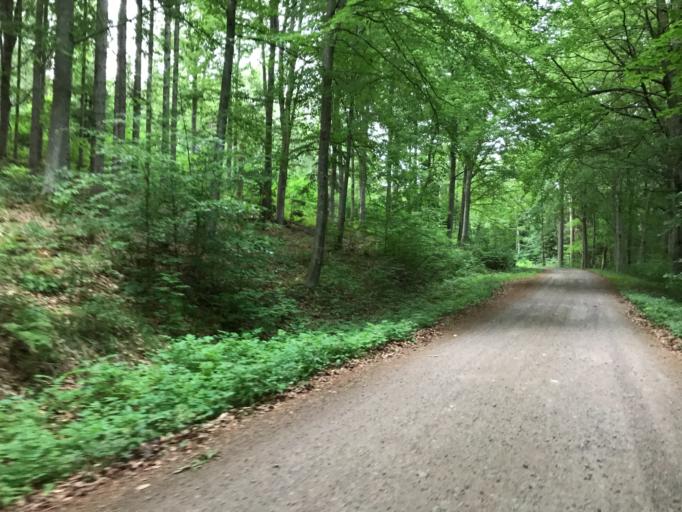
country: SE
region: OEstergoetland
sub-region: Odeshogs Kommun
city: OEdeshoeg
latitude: 58.3098
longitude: 14.6324
